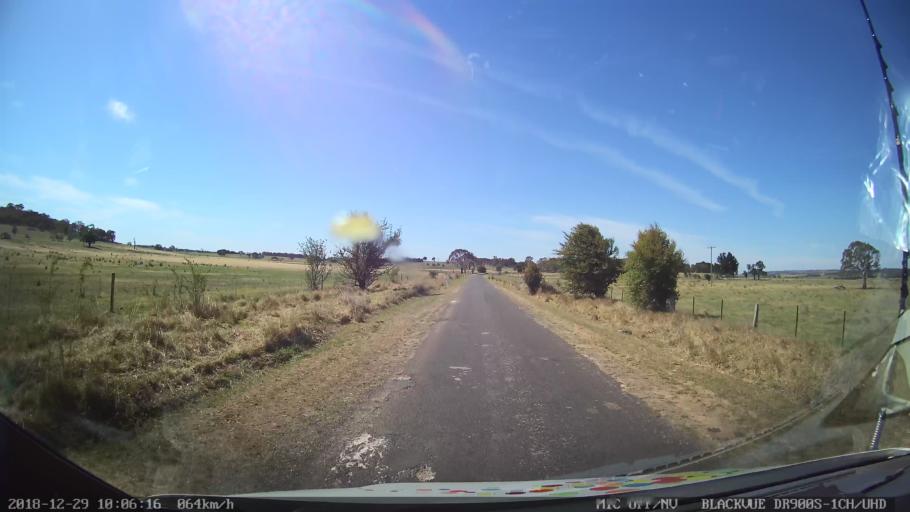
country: AU
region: New South Wales
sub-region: Yass Valley
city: Gundaroo
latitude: -34.8413
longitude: 149.4547
